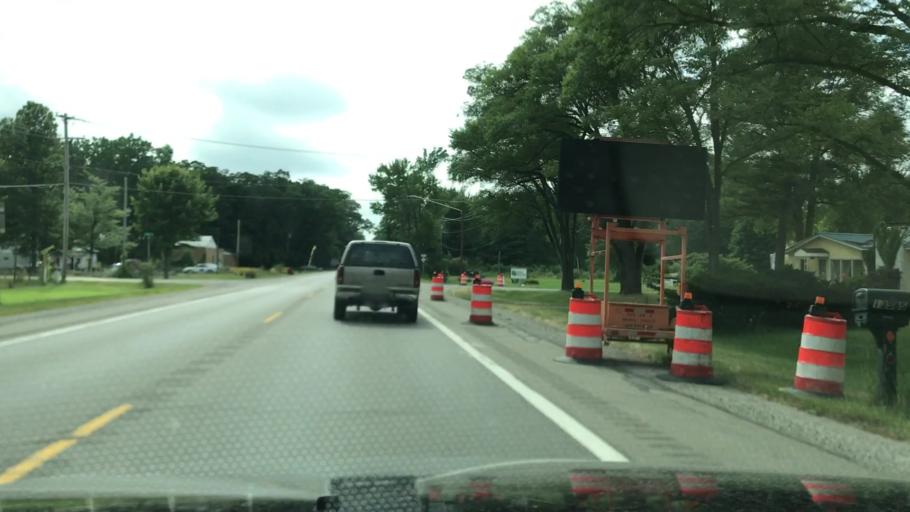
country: US
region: Michigan
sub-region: Muskegon County
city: Fruitport
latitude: 43.0739
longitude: -86.1261
